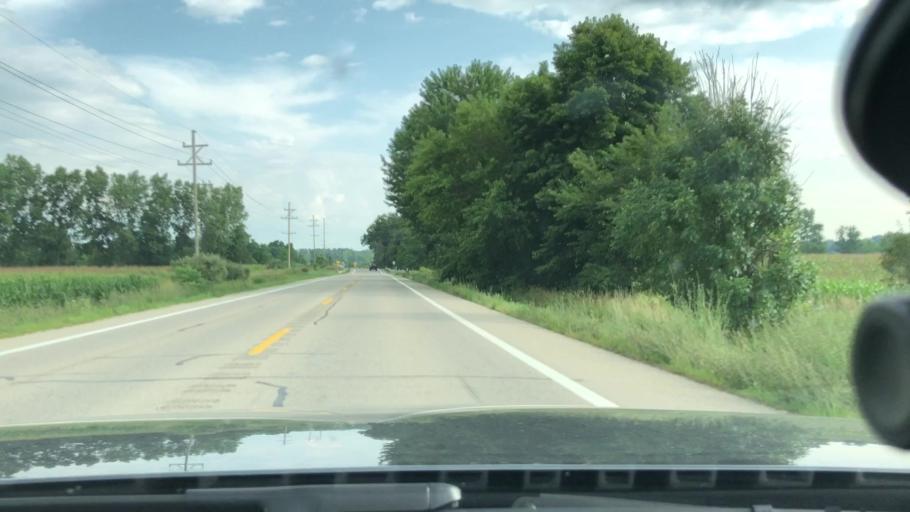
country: US
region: Michigan
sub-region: Washtenaw County
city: Chelsea
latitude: 42.2540
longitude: -84.0339
